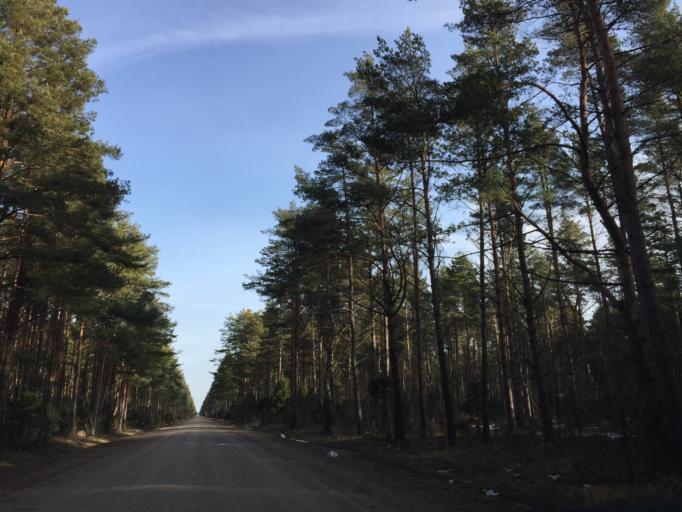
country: EE
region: Saare
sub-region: Kuressaare linn
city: Kuressaare
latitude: 58.2881
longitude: 21.9320
